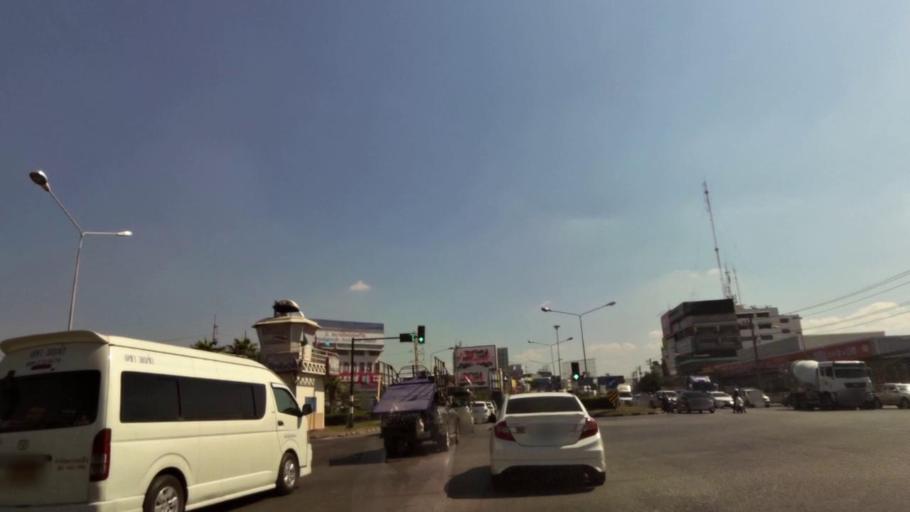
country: TH
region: Nakhon Sawan
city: Nakhon Sawan
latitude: 15.6985
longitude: 100.1201
